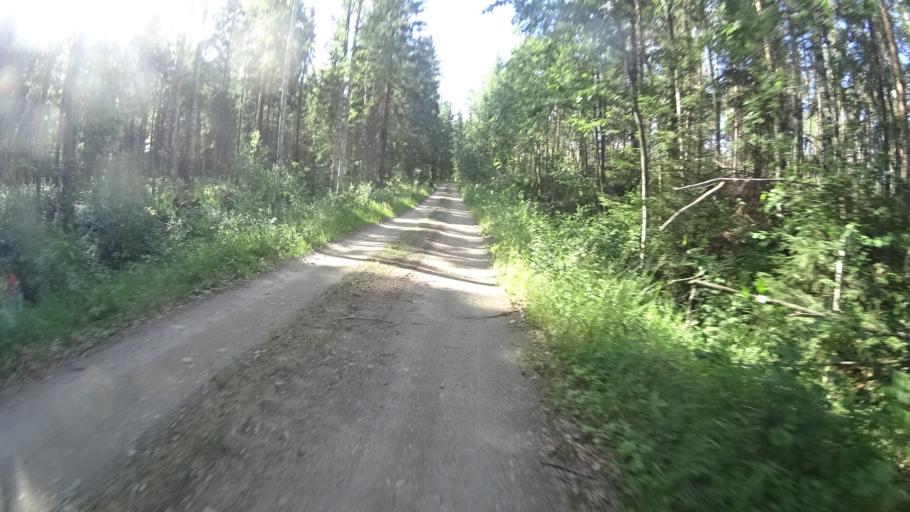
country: FI
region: Uusimaa
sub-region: Helsinki
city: Karkkila
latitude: 60.6377
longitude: 24.1632
